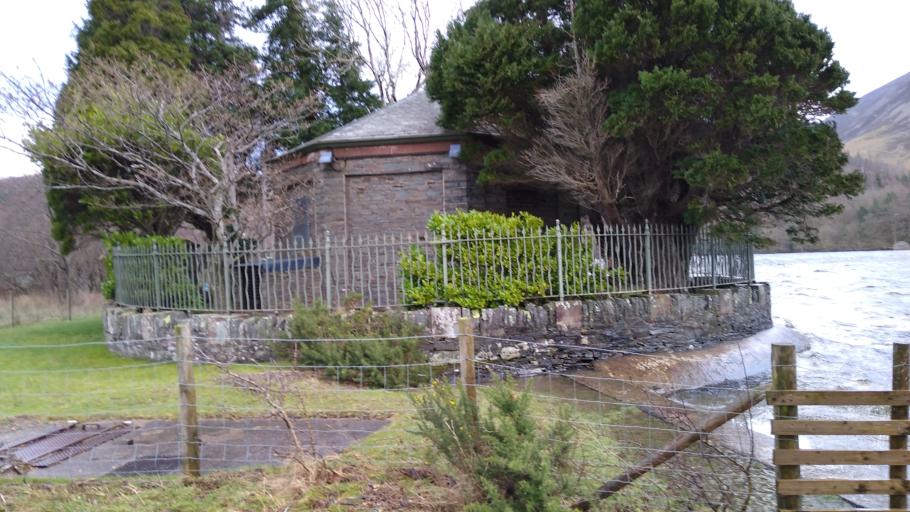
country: GB
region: England
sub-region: Cumbria
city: Cockermouth
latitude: 54.5723
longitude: -3.3146
